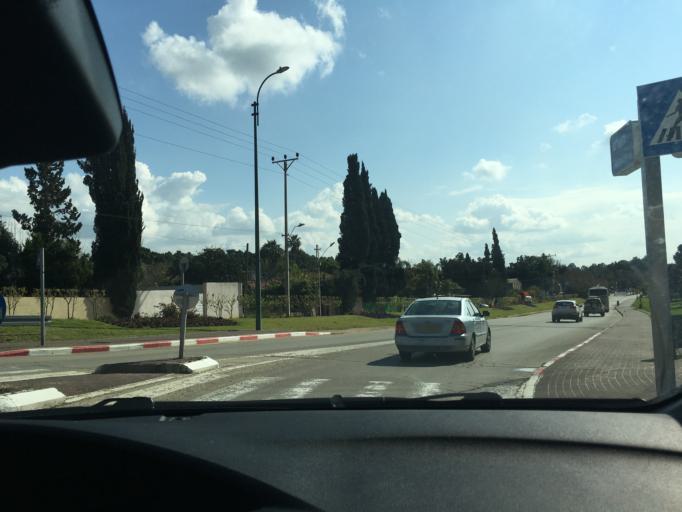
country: IL
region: Tel Aviv
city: Ramat HaSharon
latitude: 32.1658
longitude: 34.8529
